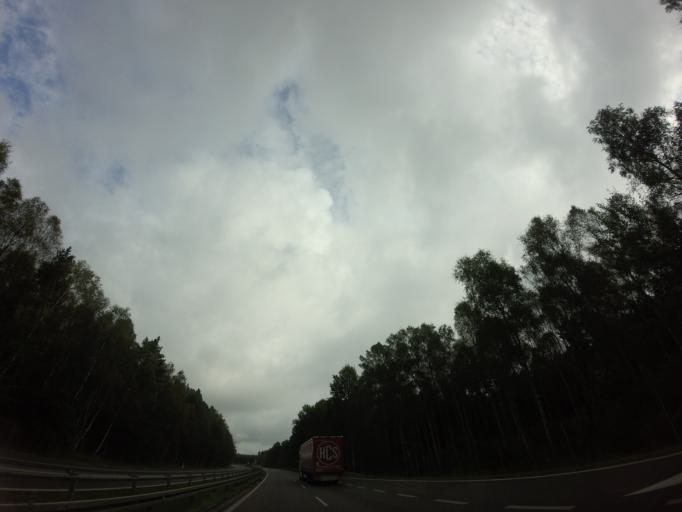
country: PL
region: West Pomeranian Voivodeship
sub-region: Powiat goleniowski
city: Goleniow
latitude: 53.5922
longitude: 14.8237
